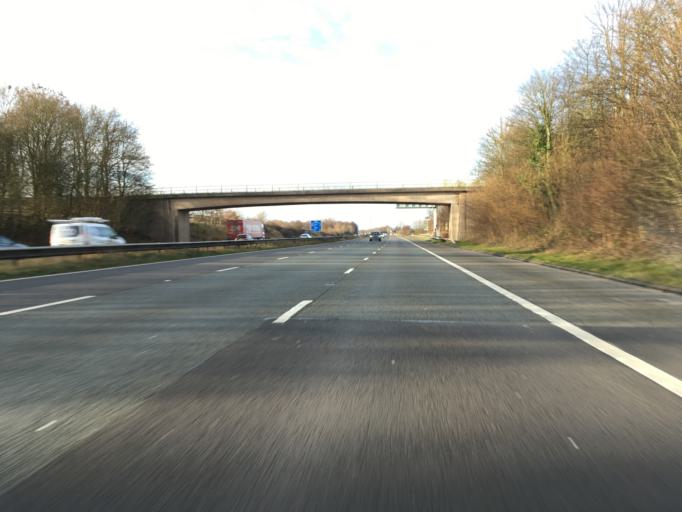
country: GB
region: England
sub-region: Cheshire East
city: Mere
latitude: 53.3641
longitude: -2.4001
